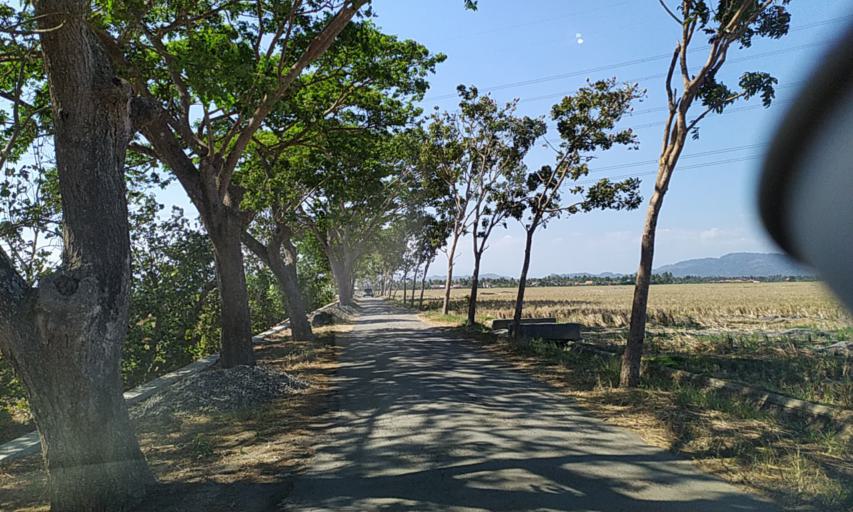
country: ID
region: Central Java
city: Mernek
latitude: -7.6042
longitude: 109.1707
